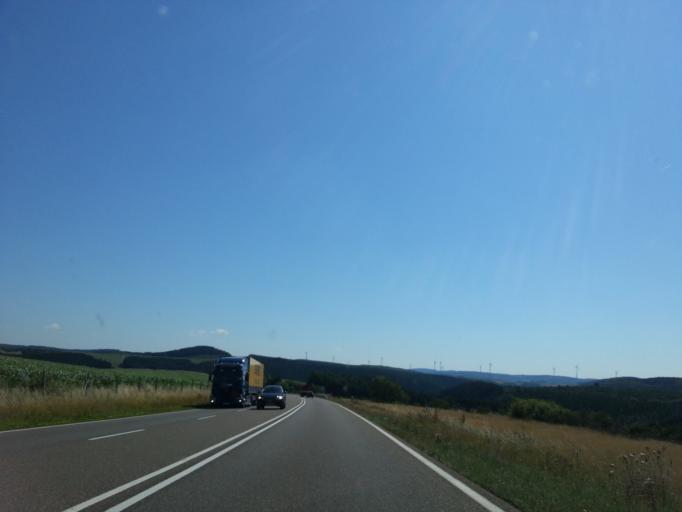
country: DE
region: Rheinland-Pfalz
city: Habscheid
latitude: 50.1981
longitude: 6.2676
